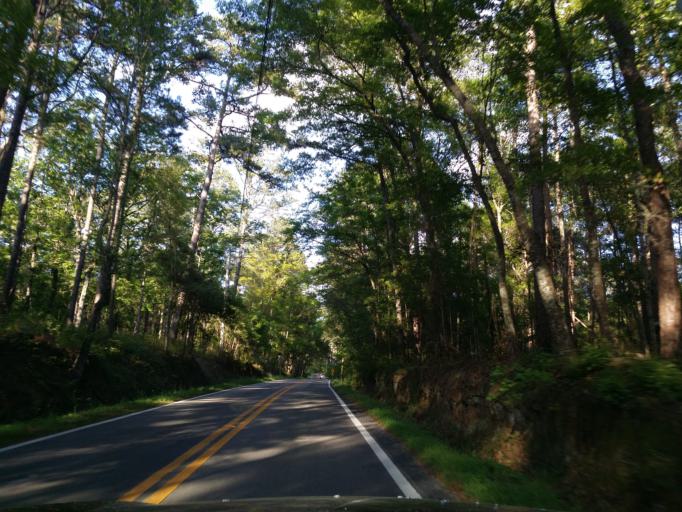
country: US
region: Florida
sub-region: Leon County
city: Tallahassee
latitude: 30.5131
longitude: -84.1388
